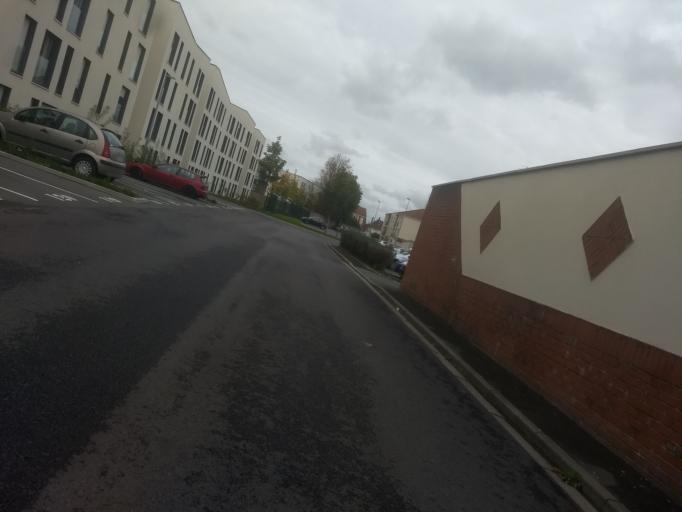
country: FR
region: Nord-Pas-de-Calais
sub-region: Departement du Pas-de-Calais
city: Arras
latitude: 50.2877
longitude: 2.7886
